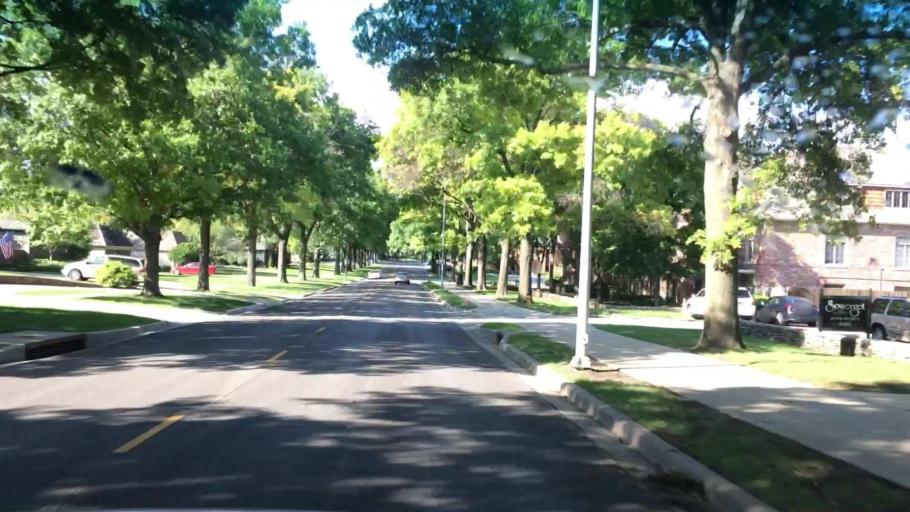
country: US
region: Kansas
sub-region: Johnson County
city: Prairie Village
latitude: 38.9762
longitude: -94.6343
